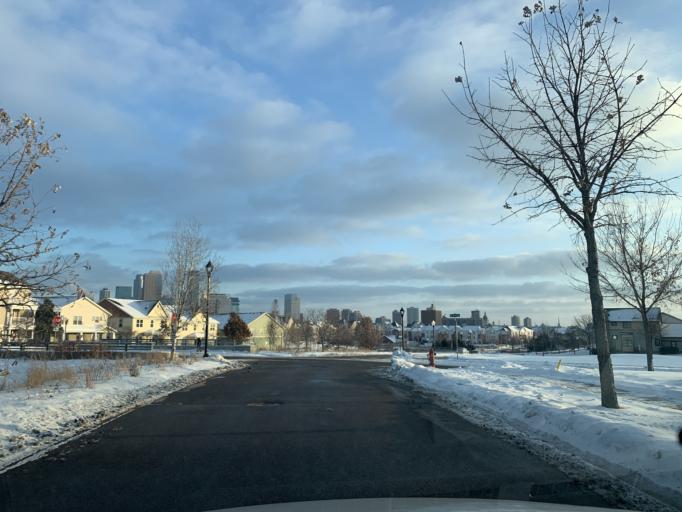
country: US
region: Minnesota
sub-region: Hennepin County
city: Minneapolis
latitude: 44.9893
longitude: -93.2932
